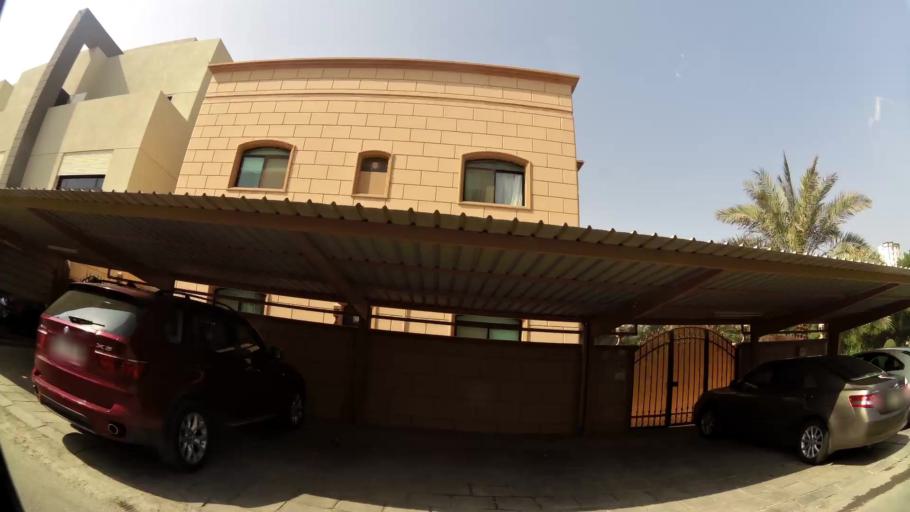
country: KW
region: Muhafazat Hawalli
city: Hawalli
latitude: 29.3503
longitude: 48.0250
